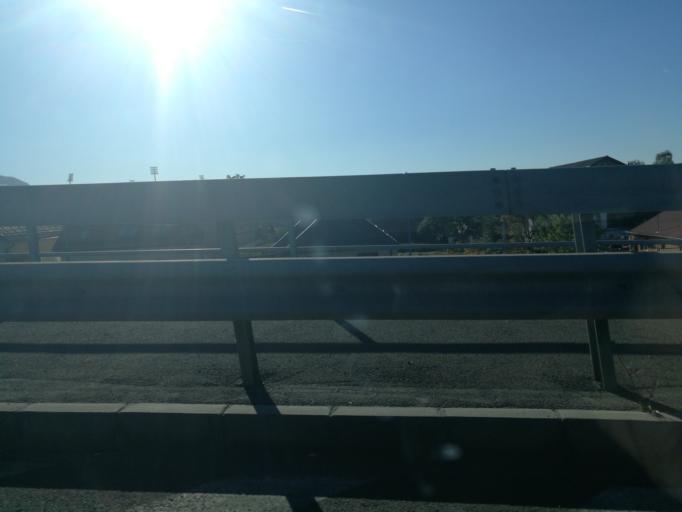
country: RO
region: Brasov
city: Brasov
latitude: 45.6681
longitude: 25.5913
